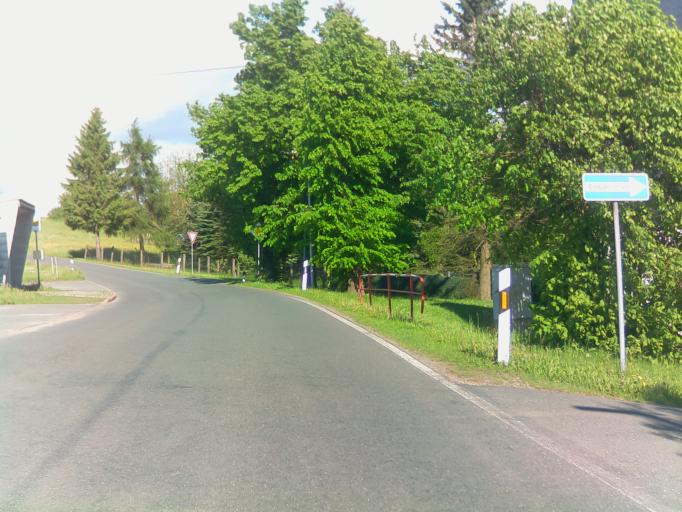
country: DE
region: Thuringia
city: Mellenbach-Glasbach
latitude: 50.6302
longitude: 11.1016
